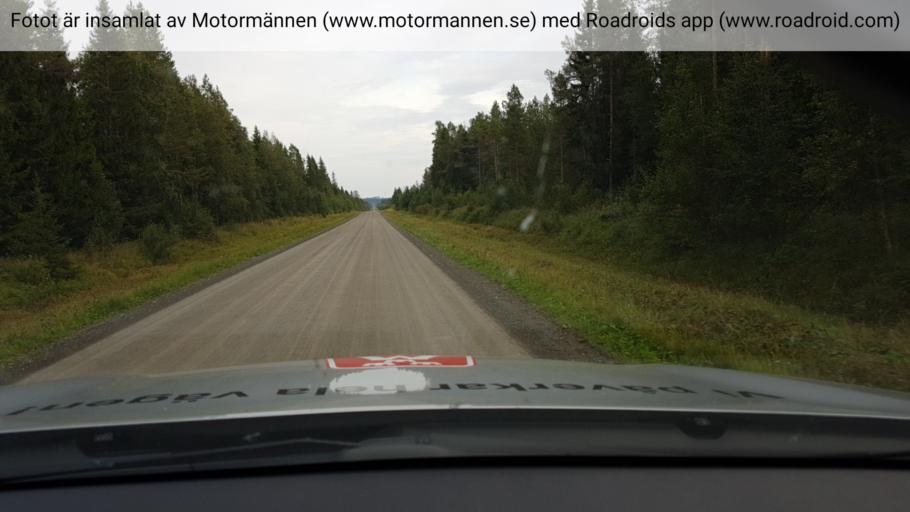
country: SE
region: Jaemtland
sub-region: OEstersunds Kommun
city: Lit
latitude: 63.6733
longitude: 14.8793
